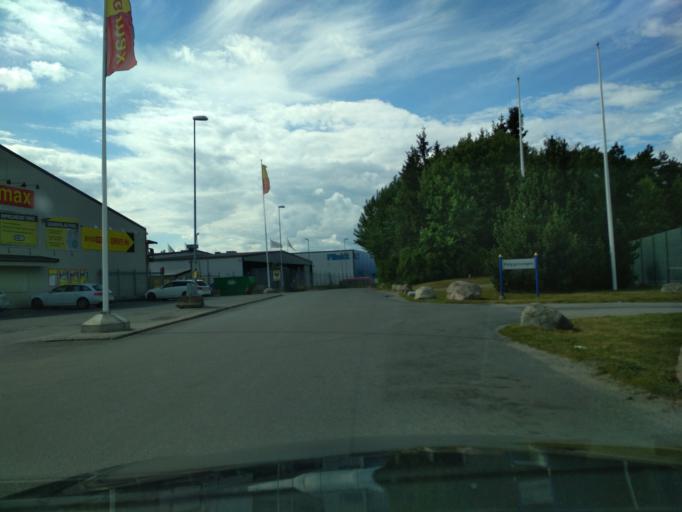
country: SE
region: Stockholm
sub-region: Taby Kommun
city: Taby
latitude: 59.4662
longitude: 18.1296
